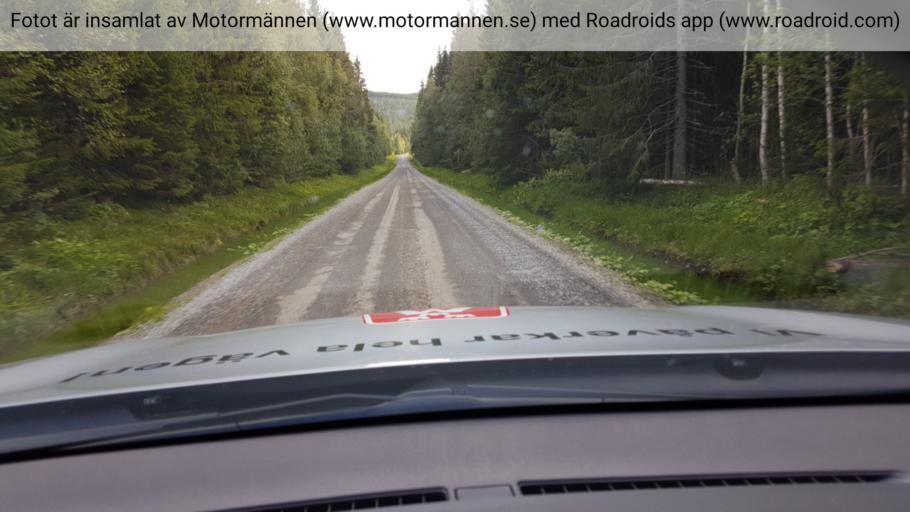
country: SE
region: Jaemtland
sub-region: Ragunda Kommun
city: Hammarstrand
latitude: 63.3168
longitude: 16.0059
